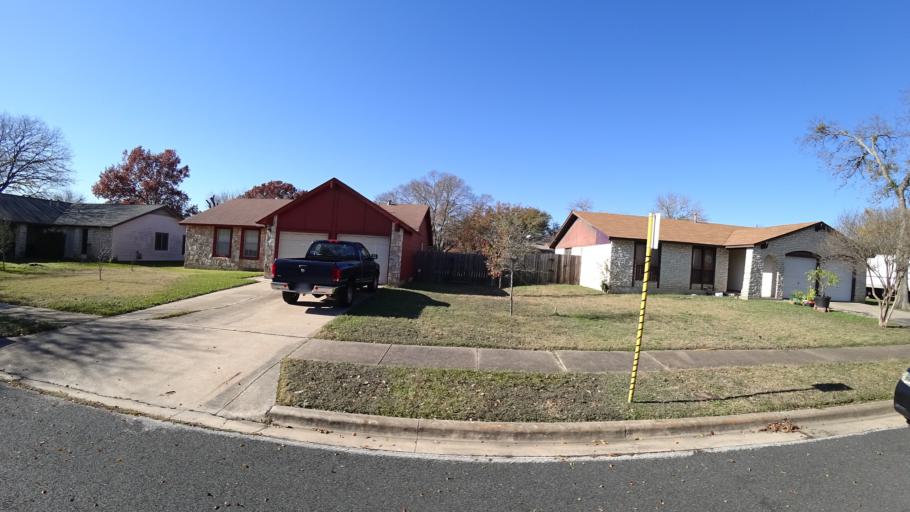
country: US
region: Texas
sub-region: Travis County
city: Wells Branch
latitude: 30.4226
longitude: -97.6899
